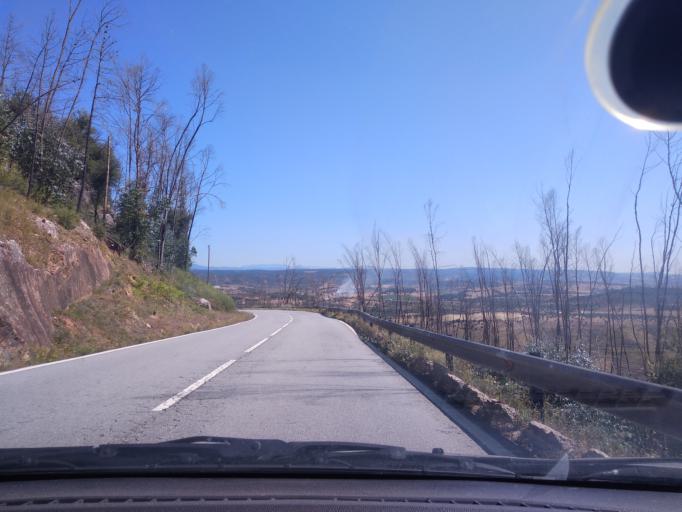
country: PT
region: Portalegre
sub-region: Nisa
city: Nisa
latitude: 39.6272
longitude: -7.6628
